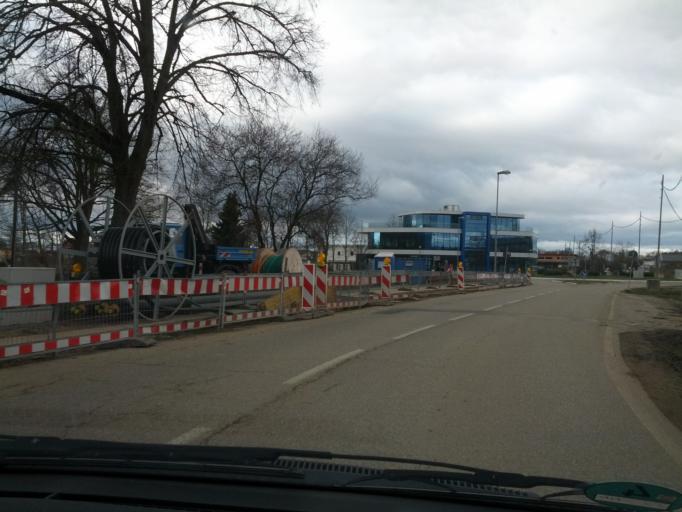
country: DE
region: Baden-Wuerttemberg
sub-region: Freiburg Region
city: Eschbach
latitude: 47.9001
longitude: 7.6336
